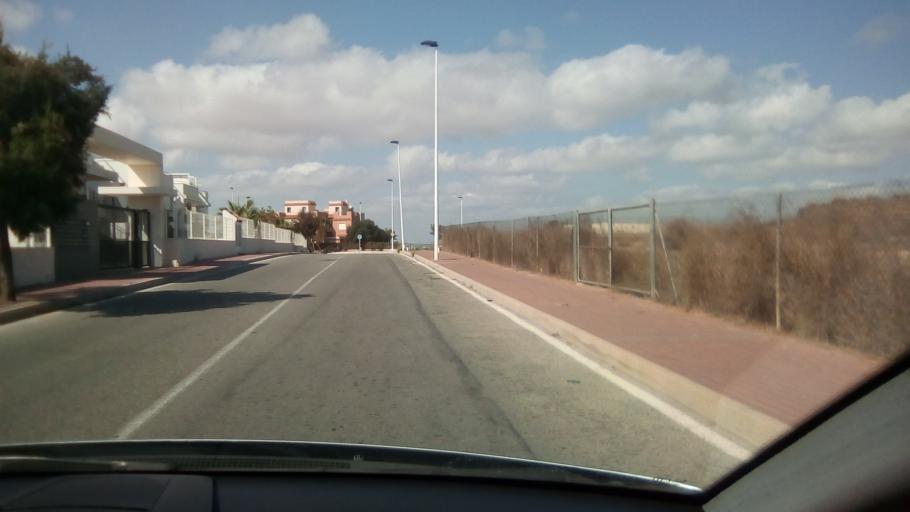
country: ES
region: Valencia
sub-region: Provincia de Alicante
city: Torrevieja
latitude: 38.0057
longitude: -0.6680
